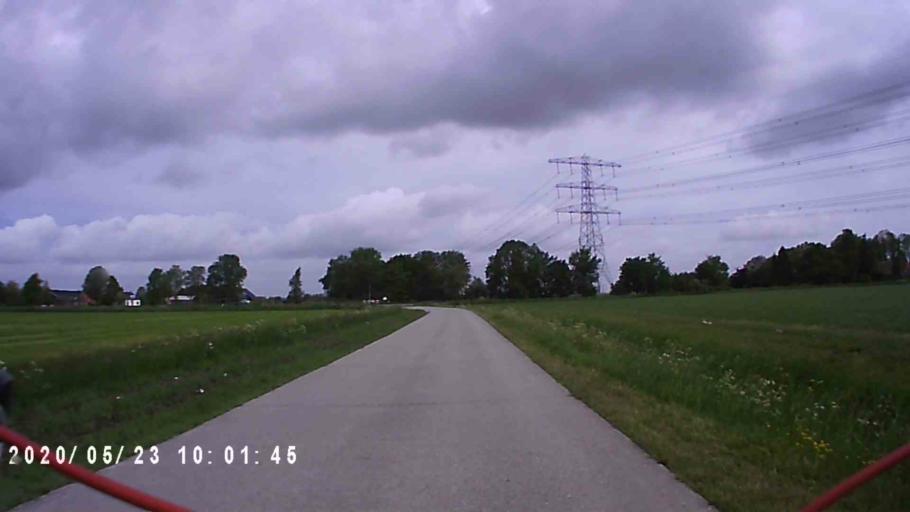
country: NL
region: Groningen
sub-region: Gemeente Appingedam
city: Appingedam
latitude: 53.3167
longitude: 6.8195
